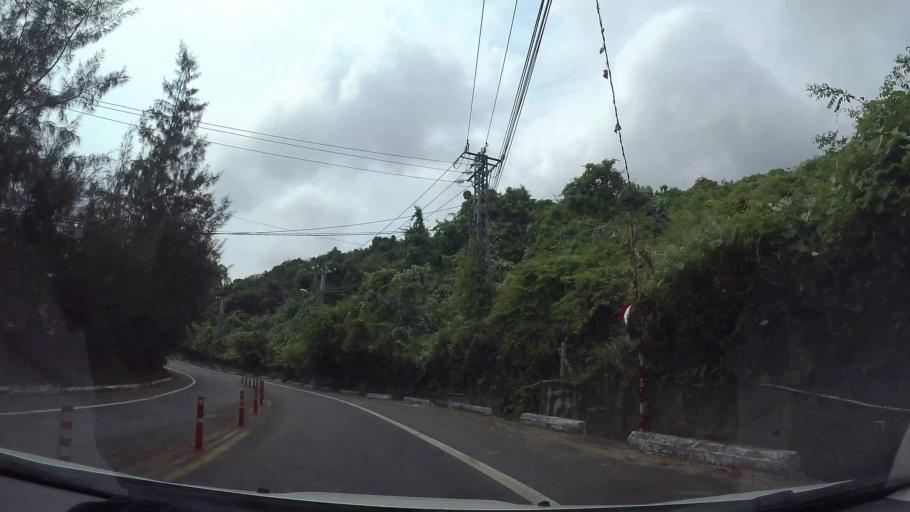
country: VN
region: Da Nang
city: Son Tra
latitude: 16.1065
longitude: 108.2952
